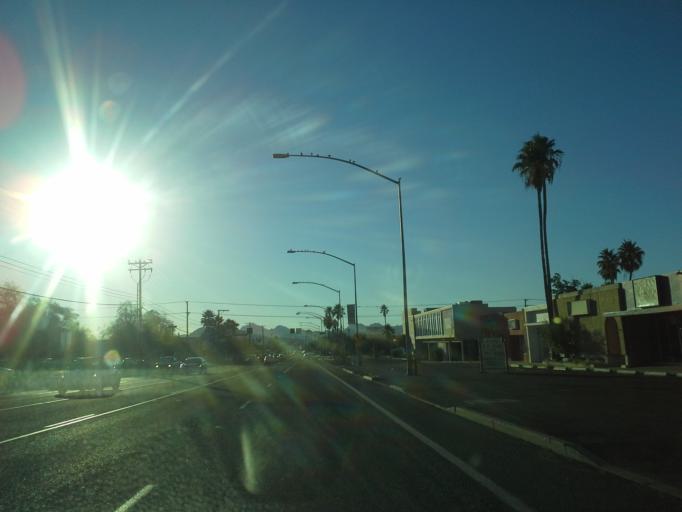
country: US
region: Arizona
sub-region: Pima County
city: Tucson
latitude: 32.2216
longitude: -110.9379
